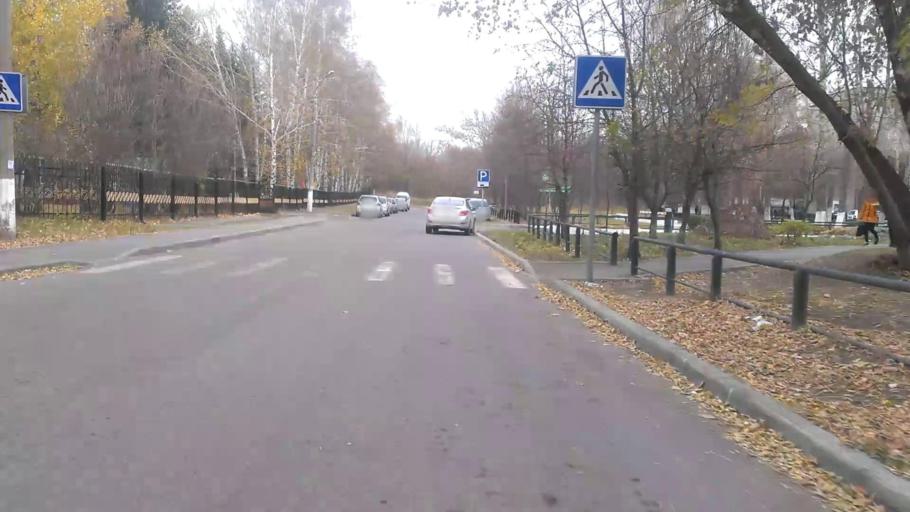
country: RU
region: Altai Krai
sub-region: Gorod Barnaulskiy
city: Barnaul
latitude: 53.3663
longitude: 83.7184
